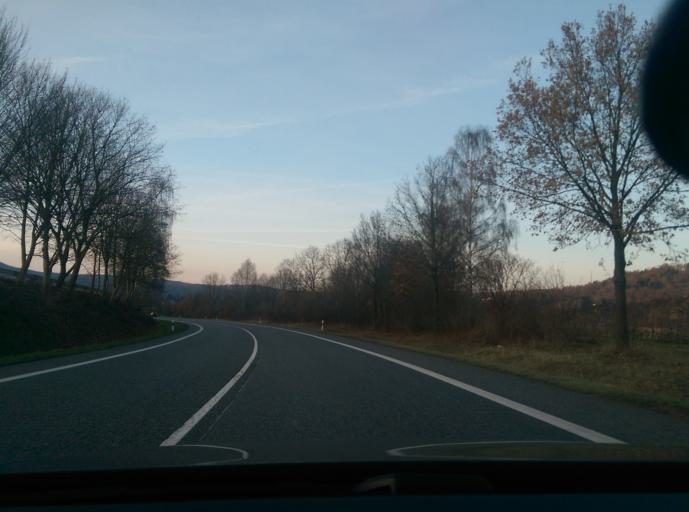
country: DE
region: Hesse
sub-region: Regierungsbezirk Kassel
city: Bad Sooden-Allendorf
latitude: 51.2561
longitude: 9.9959
